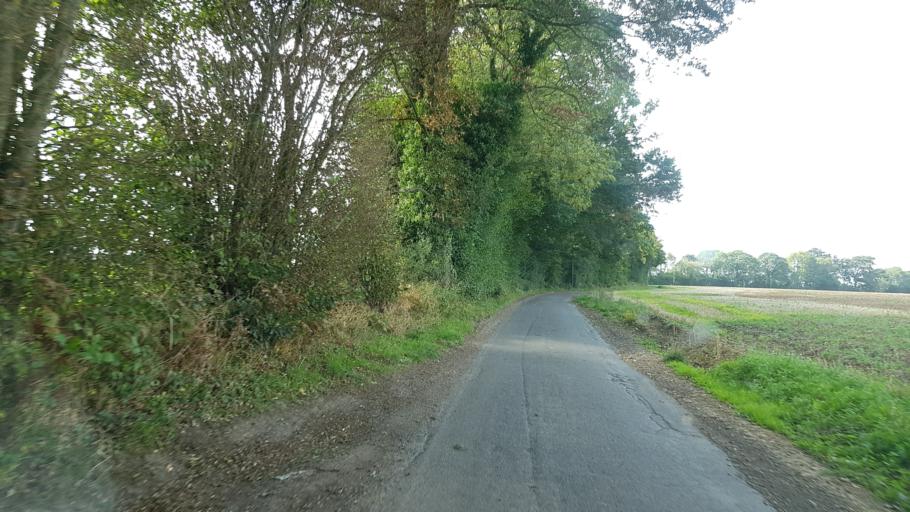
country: GB
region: England
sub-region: Kent
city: Harrietsham
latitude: 51.2400
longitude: 0.6160
